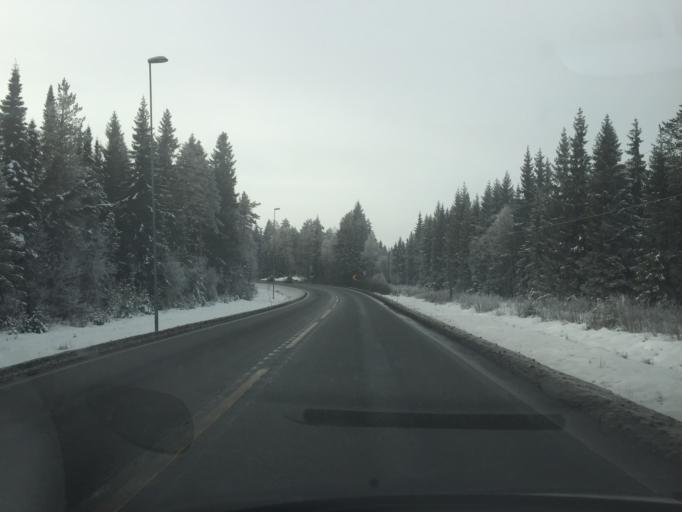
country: NO
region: Hedmark
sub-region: Loten
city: Loten
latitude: 60.8706
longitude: 11.4321
